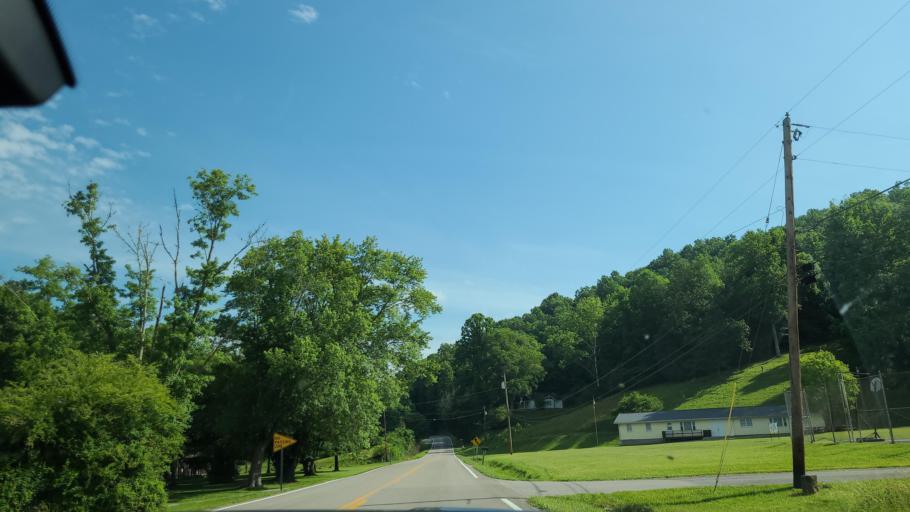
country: US
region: Kentucky
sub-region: Bell County
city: Pineville
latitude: 36.7308
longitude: -83.7976
